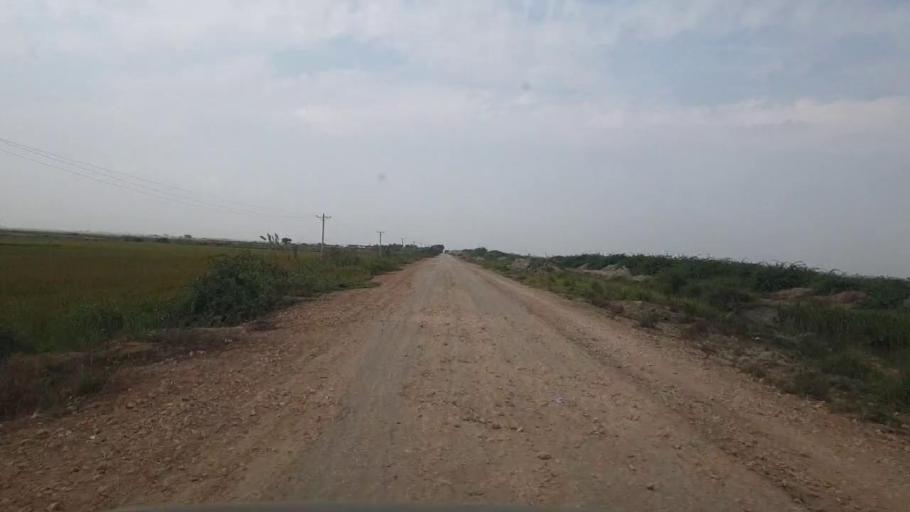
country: PK
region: Sindh
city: Kario
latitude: 24.6179
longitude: 68.5852
